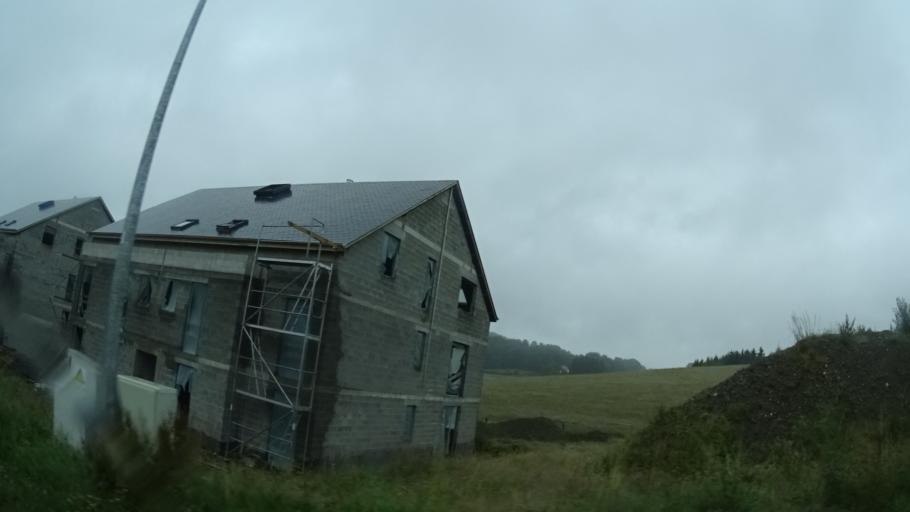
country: BE
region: Wallonia
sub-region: Province du Luxembourg
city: Leglise
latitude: 49.7977
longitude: 5.5404
